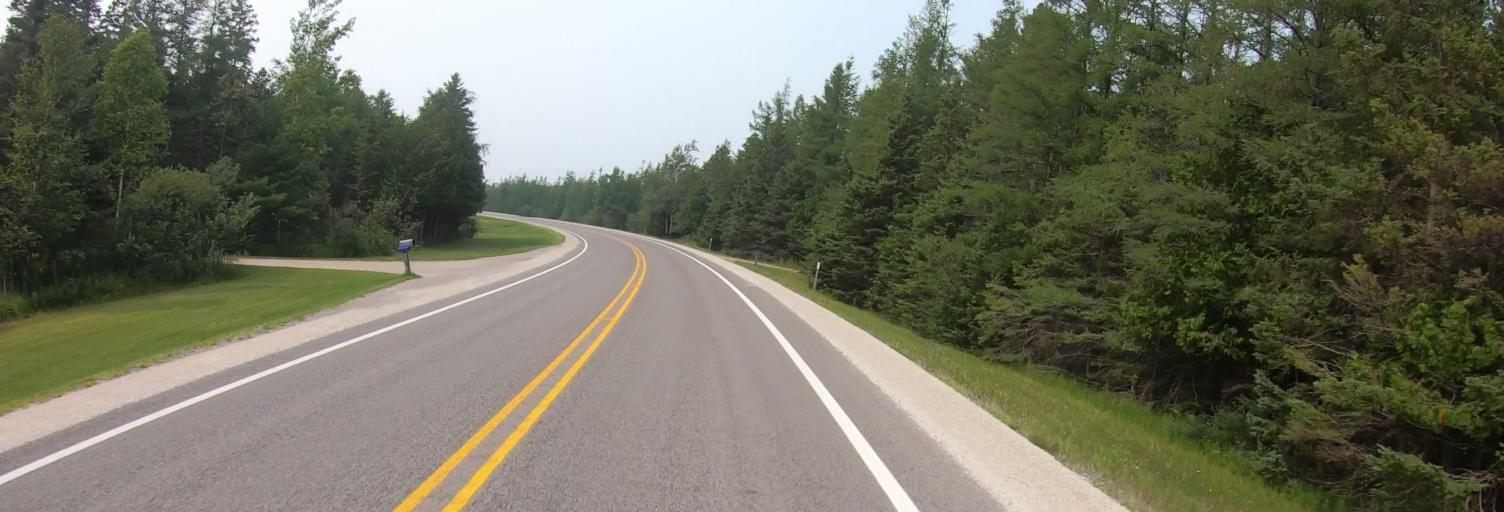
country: US
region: Michigan
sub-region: Chippewa County
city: Sault Ste. Marie
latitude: 46.0711
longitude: -84.0929
